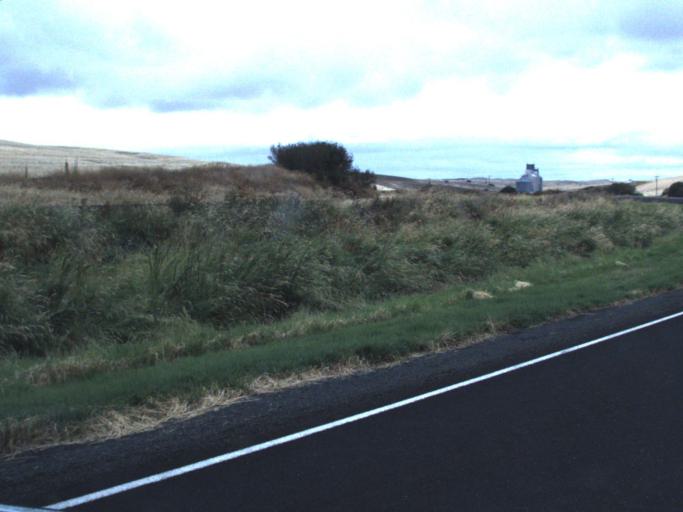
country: US
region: Washington
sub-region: Whitman County
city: Colfax
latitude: 47.1835
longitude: -117.2963
